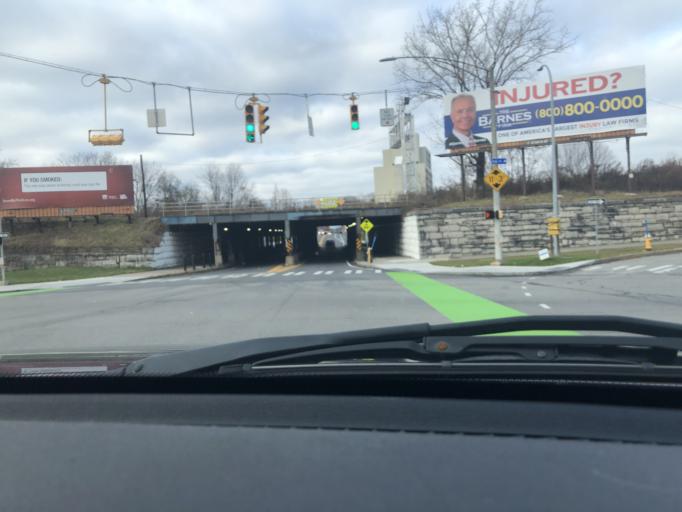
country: US
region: New York
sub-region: Monroe County
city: Rochester
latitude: 43.1616
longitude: -77.6106
